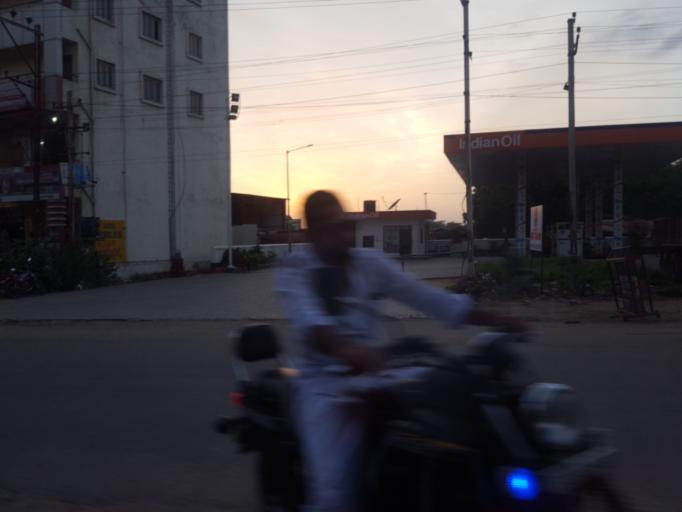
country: IN
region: Telangana
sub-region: Medak
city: Serilingampalle
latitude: 17.5300
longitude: 78.3558
